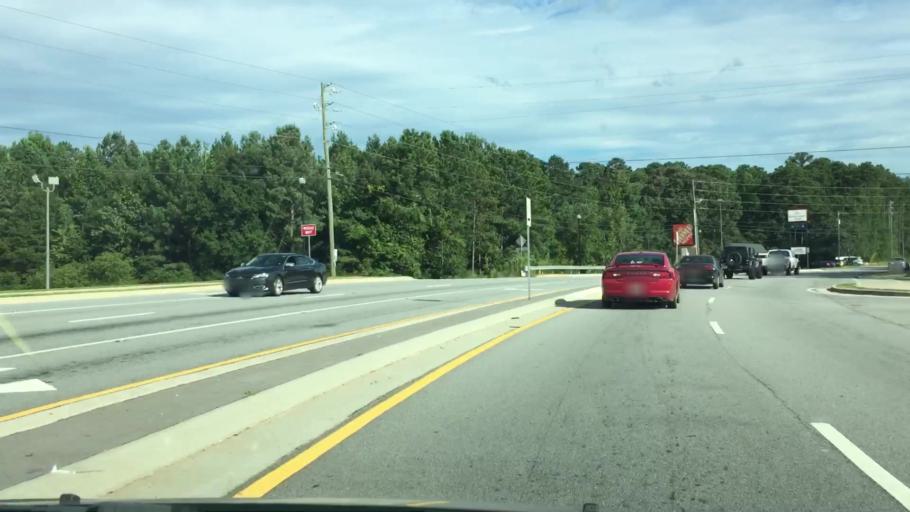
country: US
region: Georgia
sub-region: Henry County
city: Stockbridge
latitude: 33.6204
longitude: -84.2357
